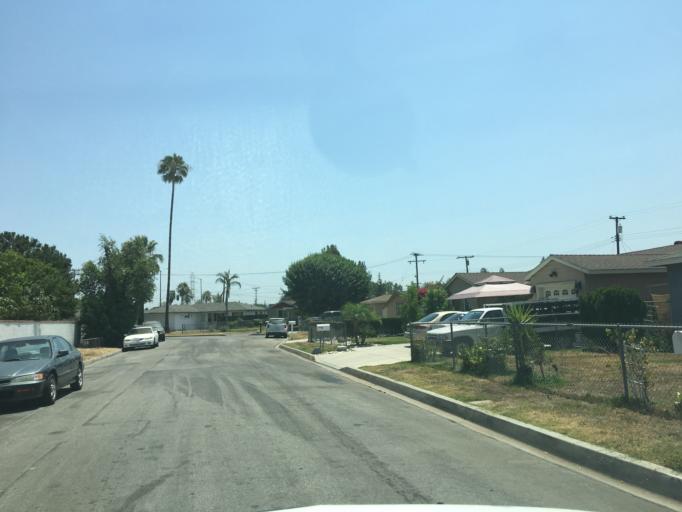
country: US
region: California
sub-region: Los Angeles County
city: Citrus
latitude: 34.1224
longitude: -117.8824
